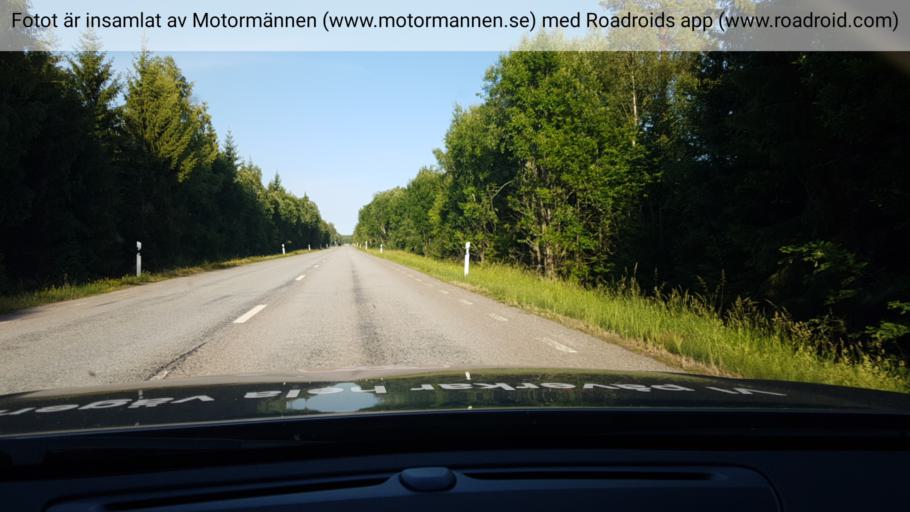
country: SE
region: Uppsala
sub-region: Osthammars Kommun
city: Gimo
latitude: 60.1651
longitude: 18.1589
